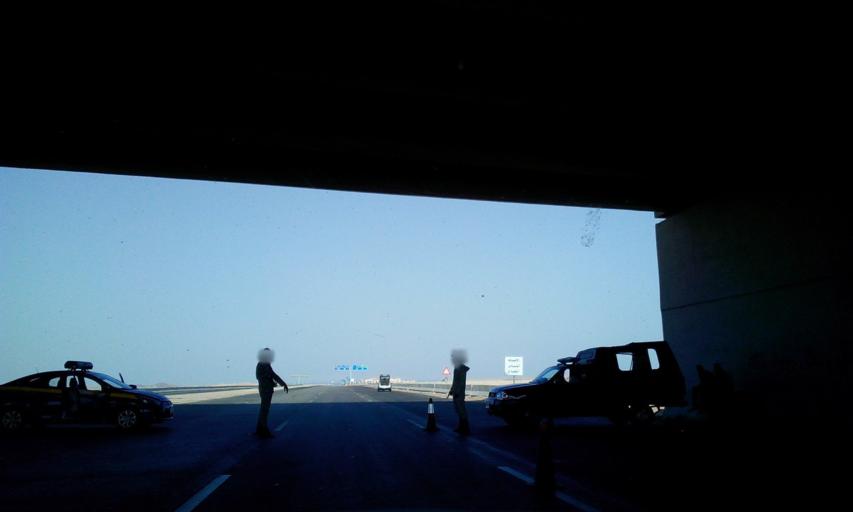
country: EG
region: As Suways
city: Ain Sukhna
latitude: 29.1089
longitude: 32.5334
